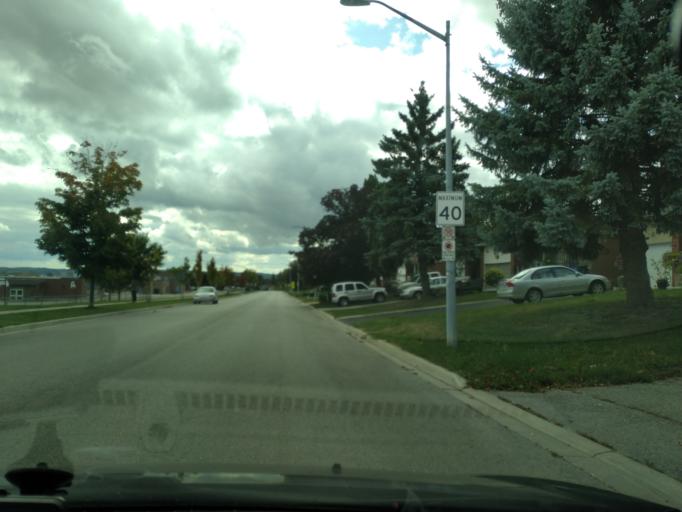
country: CA
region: Ontario
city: Bradford West Gwillimbury
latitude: 44.1200
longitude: -79.5619
